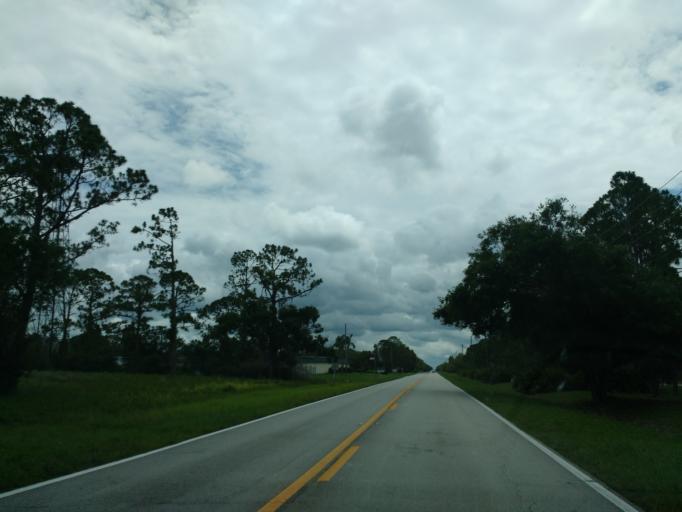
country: US
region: Florida
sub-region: Highlands County
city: Sebring
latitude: 27.4709
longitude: -81.5122
